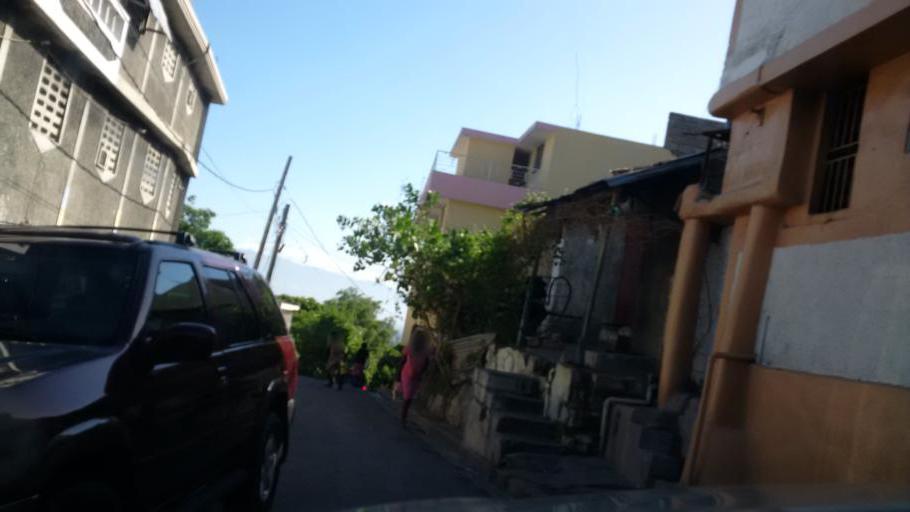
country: HT
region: Ouest
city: Delmas 73
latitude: 18.5431
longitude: -72.3154
